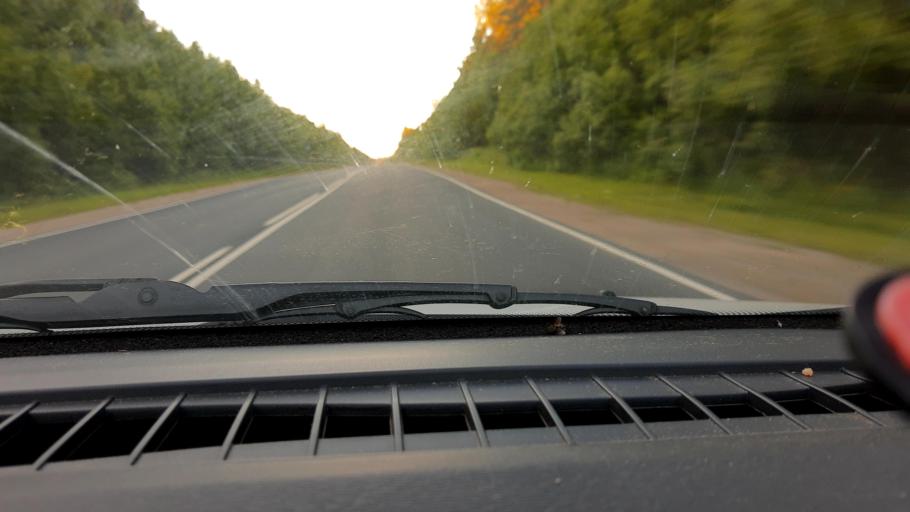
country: RU
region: Nizjnij Novgorod
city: Vladimirskoye
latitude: 56.9453
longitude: 45.0835
